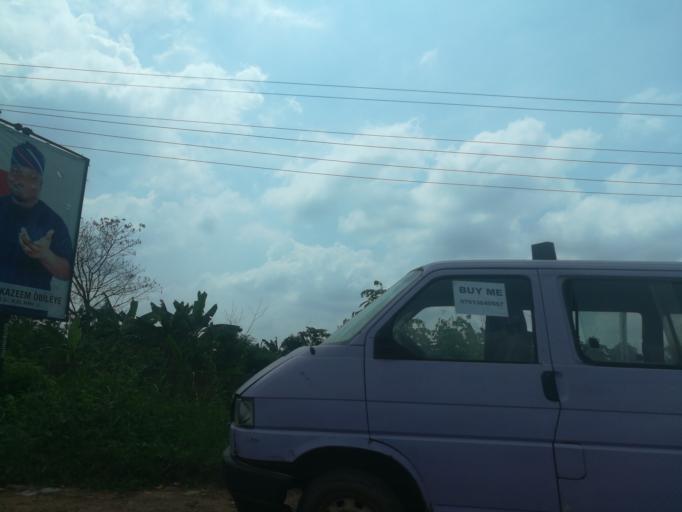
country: NG
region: Oyo
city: Ibadan
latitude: 7.3832
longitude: 3.8331
